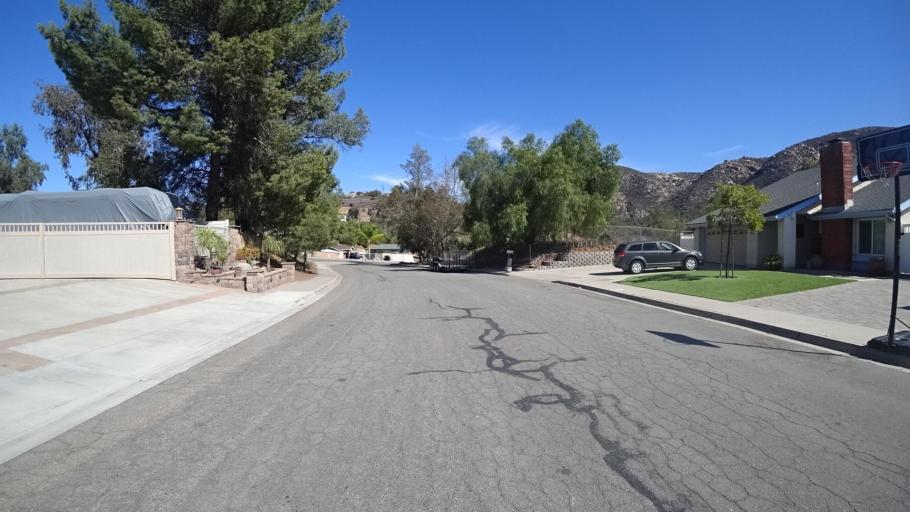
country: US
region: California
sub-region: San Diego County
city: Crest
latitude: 32.8489
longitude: -116.8652
